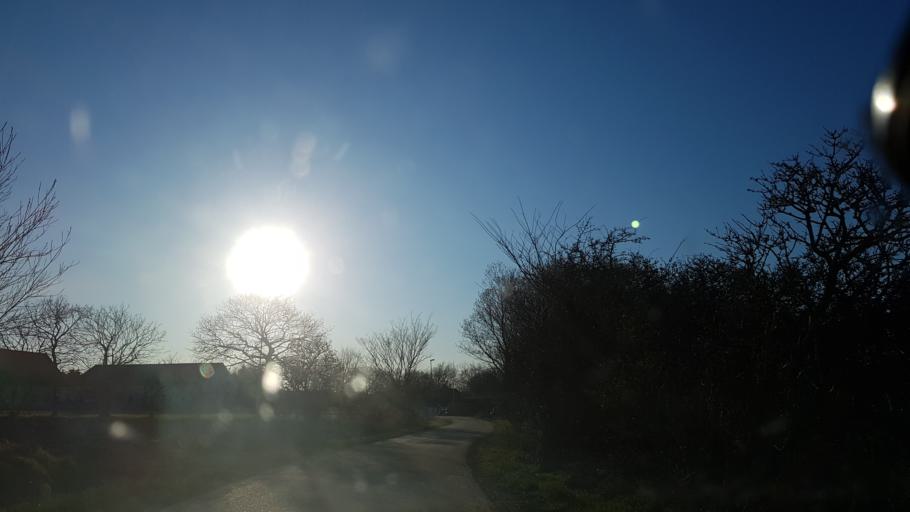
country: DK
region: South Denmark
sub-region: Esbjerg Kommune
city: Bramming
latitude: 55.4209
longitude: 8.6452
